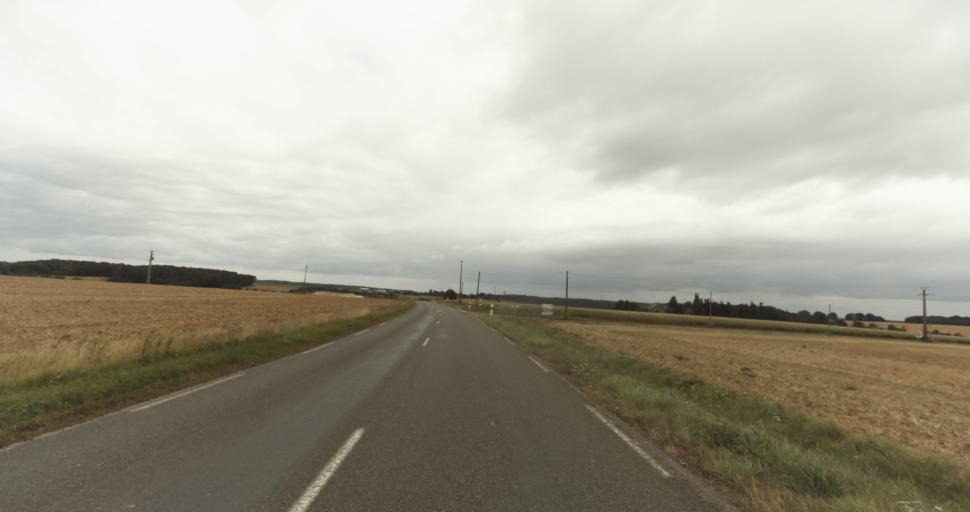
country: FR
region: Haute-Normandie
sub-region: Departement de l'Eure
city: Gravigny
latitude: 49.0544
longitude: 1.2425
